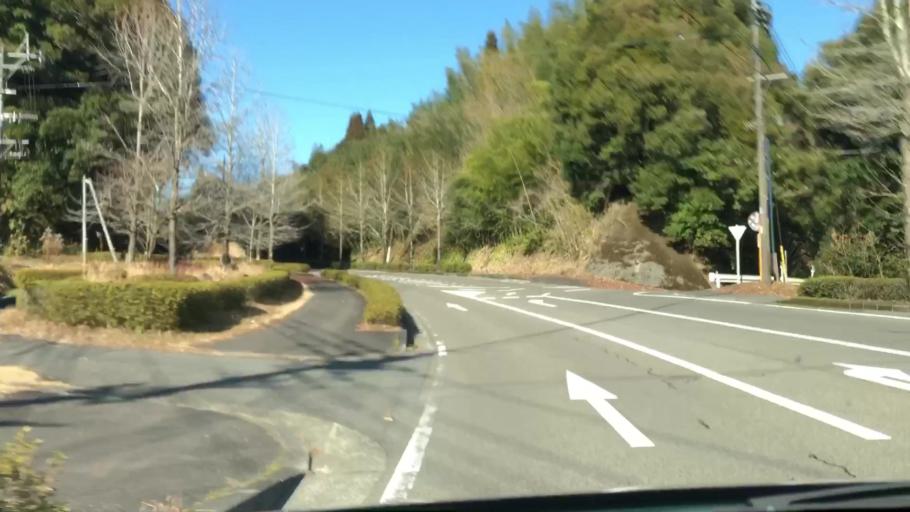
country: JP
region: Kagoshima
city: Satsumasendai
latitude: 31.8278
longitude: 130.4353
